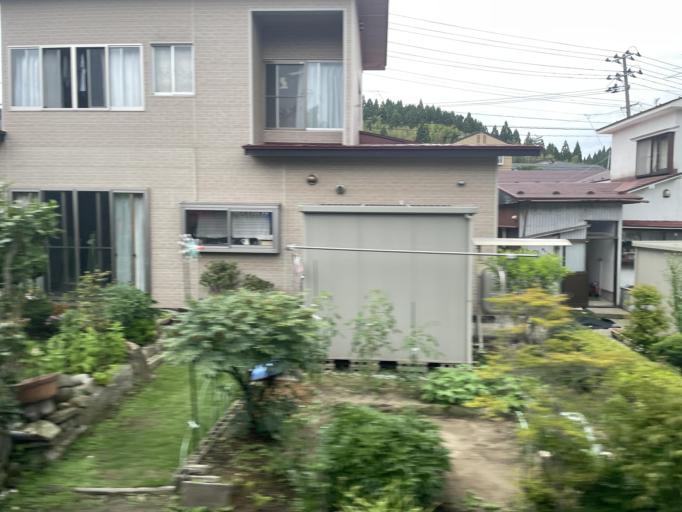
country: JP
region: Akita
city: Tenno
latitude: 39.8924
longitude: 139.8535
